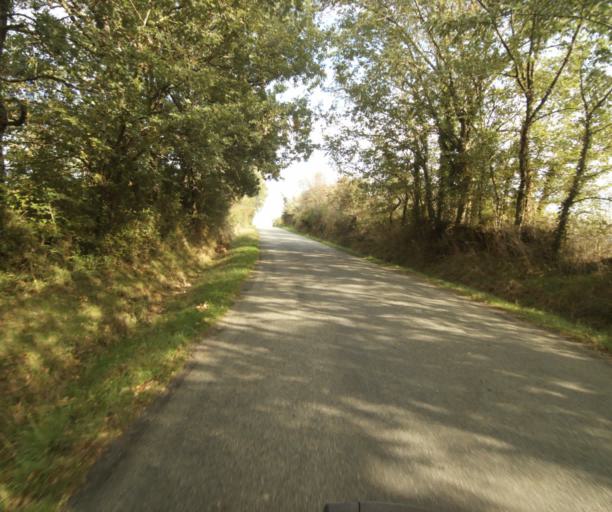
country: FR
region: Midi-Pyrenees
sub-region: Departement du Tarn-et-Garonne
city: Verdun-sur-Garonne
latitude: 43.8363
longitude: 1.1528
